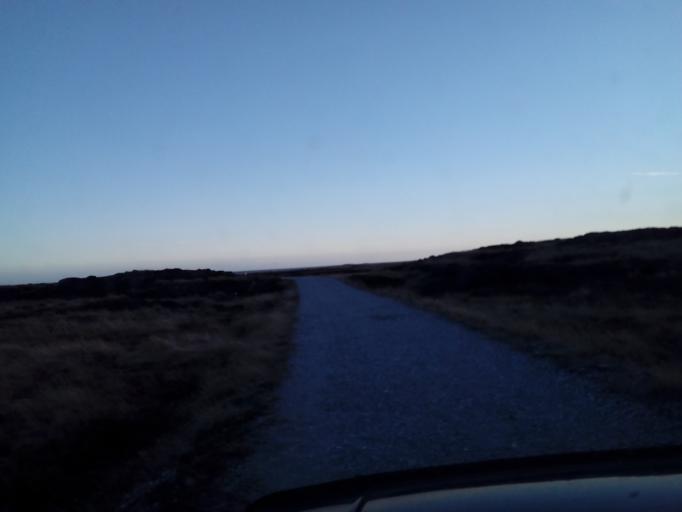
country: FK
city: Stanley
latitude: -51.7029
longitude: -57.8429
